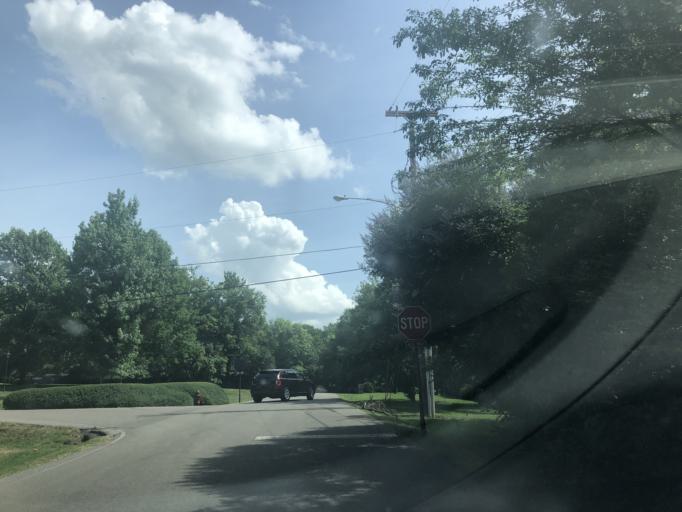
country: US
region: Tennessee
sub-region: Davidson County
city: Oak Hill
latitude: 36.0839
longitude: -86.7987
